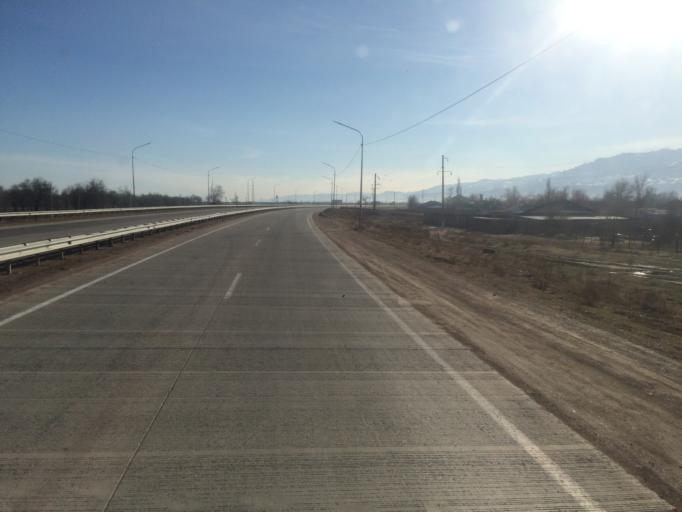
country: KG
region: Talas
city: Ivanovo-Alekseyevka
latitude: 42.9958
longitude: 72.1045
